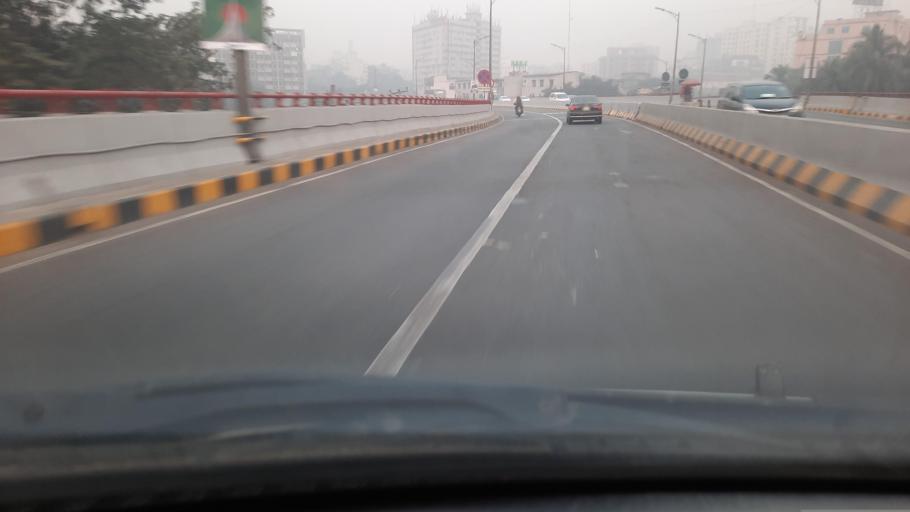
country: BD
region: Dhaka
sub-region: Dhaka
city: Dhaka
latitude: 23.7155
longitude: 90.4233
